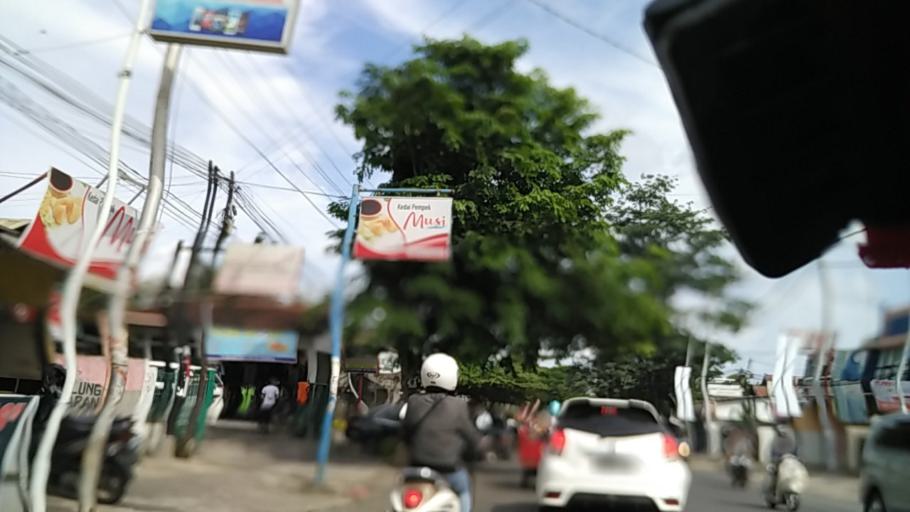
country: ID
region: Central Java
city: Semarang
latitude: -7.0509
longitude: 110.4246
